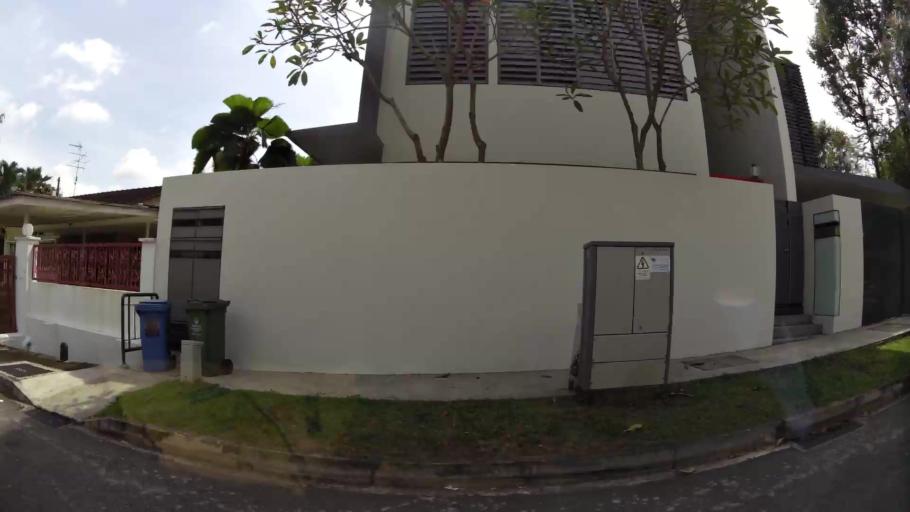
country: SG
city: Singapore
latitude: 1.3300
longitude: 103.7917
